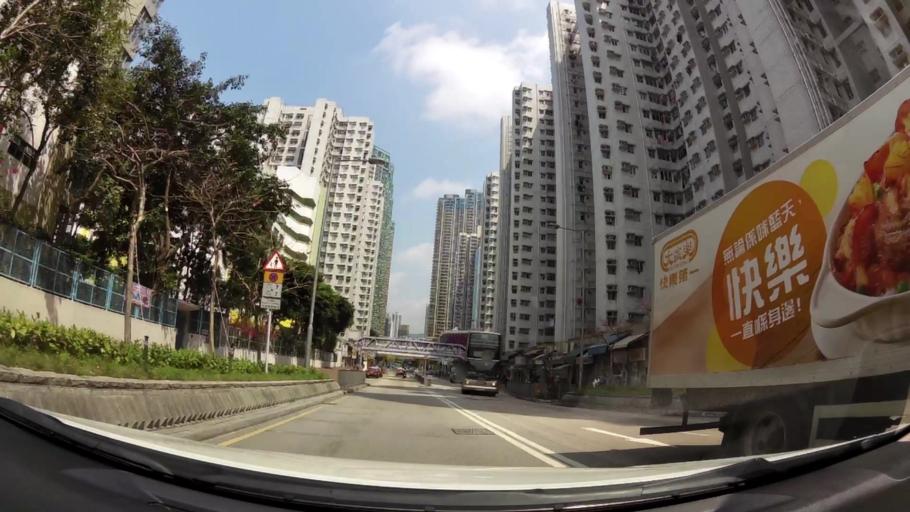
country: HK
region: Sham Shui Po
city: Sham Shui Po
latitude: 22.3135
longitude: 114.1644
